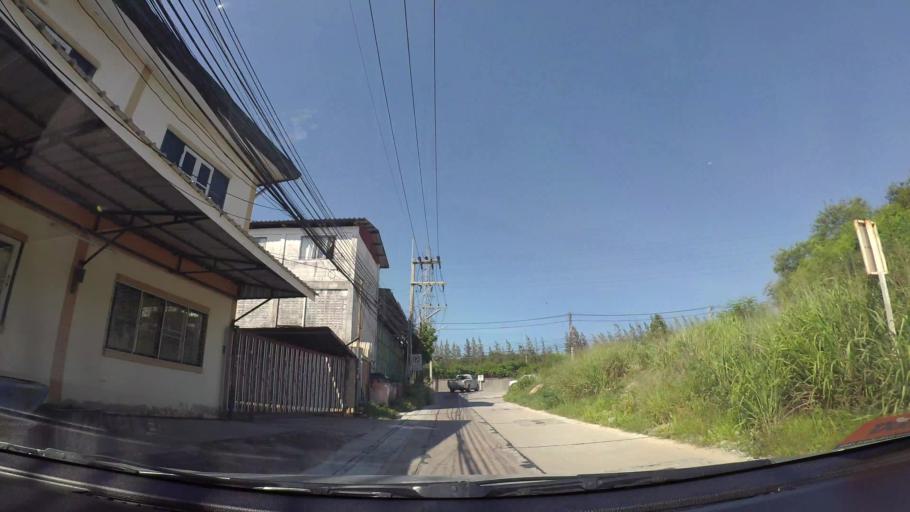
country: TH
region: Chon Buri
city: Si Racha
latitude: 13.1561
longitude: 100.9412
